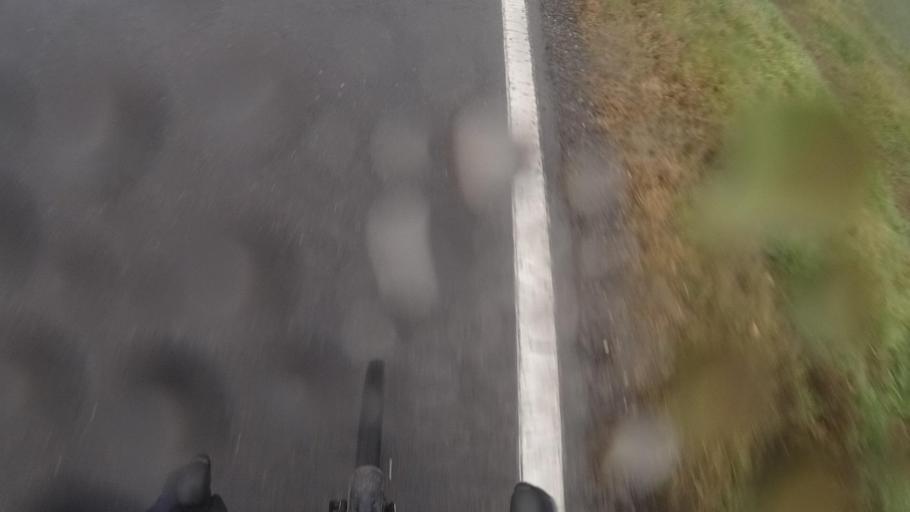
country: DE
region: Rheinland-Pfalz
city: Karbach
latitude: 50.1628
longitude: 7.6132
